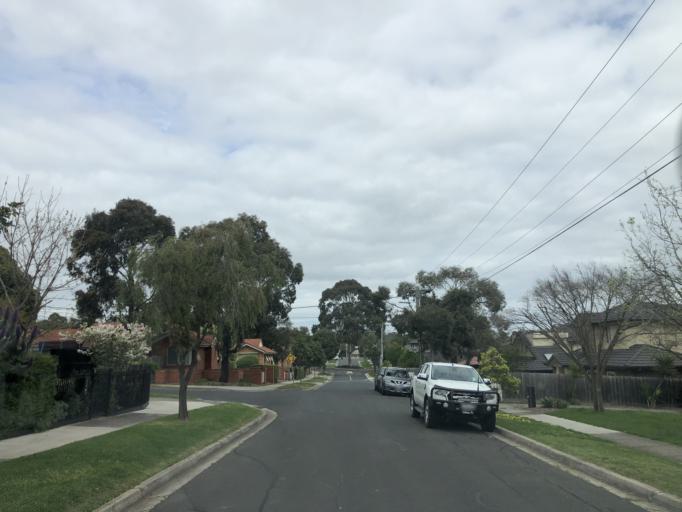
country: AU
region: Victoria
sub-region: Monash
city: Ashwood
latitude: -37.8710
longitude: 145.1026
